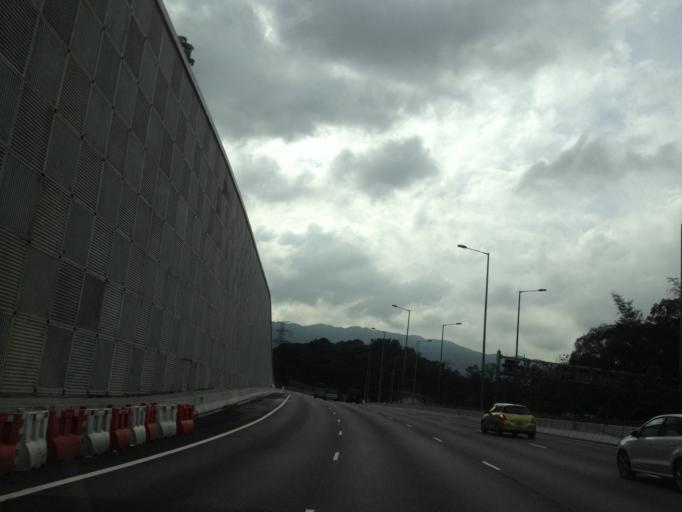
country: HK
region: Tai Po
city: Tai Po
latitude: 22.4451
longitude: 114.1573
